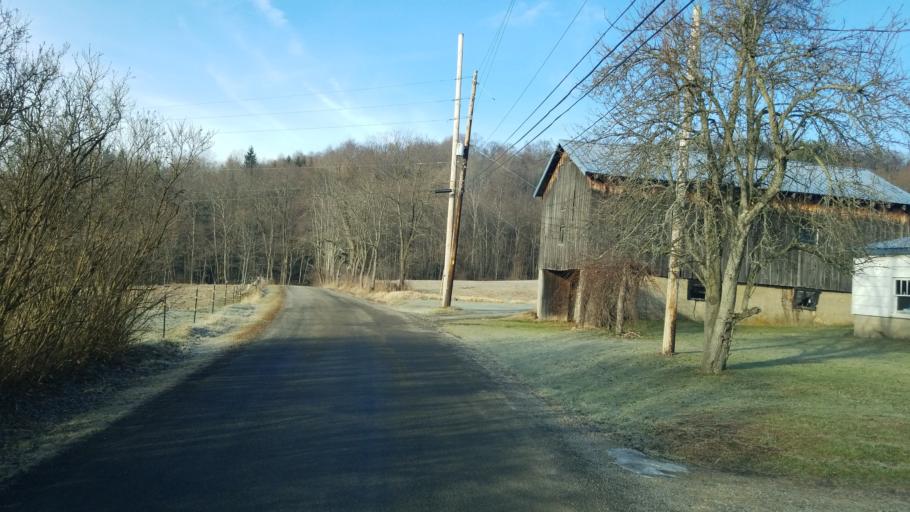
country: US
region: Pennsylvania
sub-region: Jefferson County
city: Brookville
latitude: 40.9581
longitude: -79.2625
